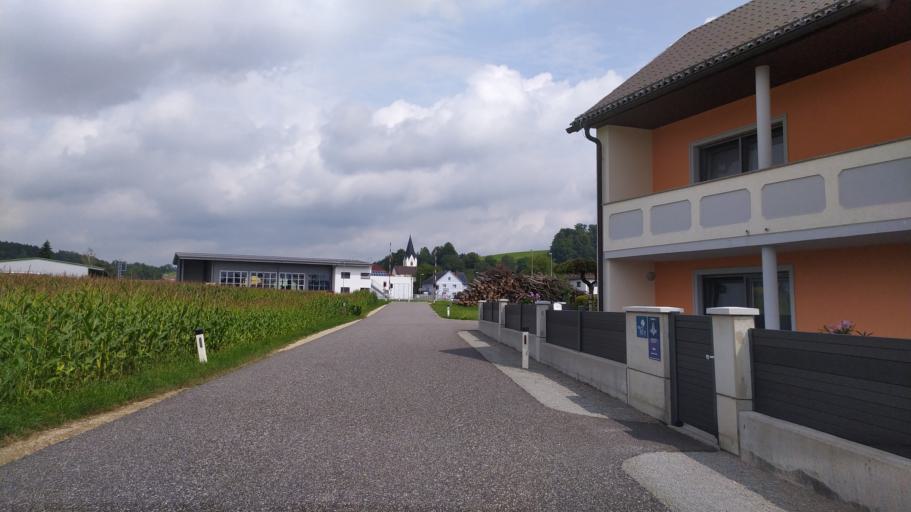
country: AT
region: Upper Austria
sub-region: Politischer Bezirk Perg
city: Bad Kreuzen
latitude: 48.2048
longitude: 14.7876
